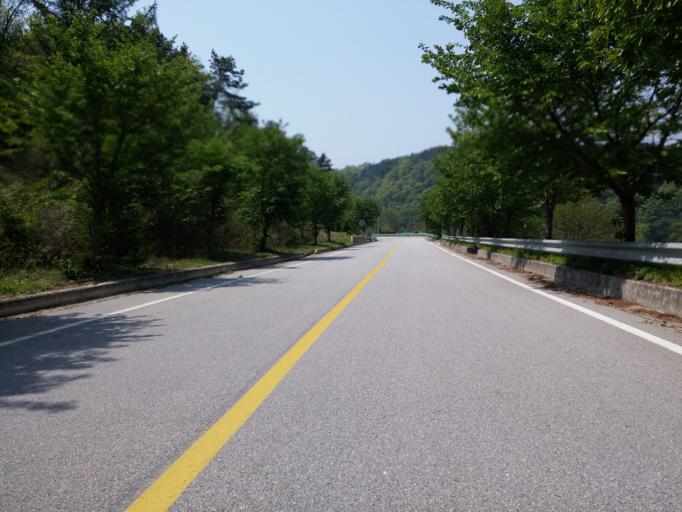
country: KR
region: Chungcheongbuk-do
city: Okcheon
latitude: 36.4313
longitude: 127.5748
